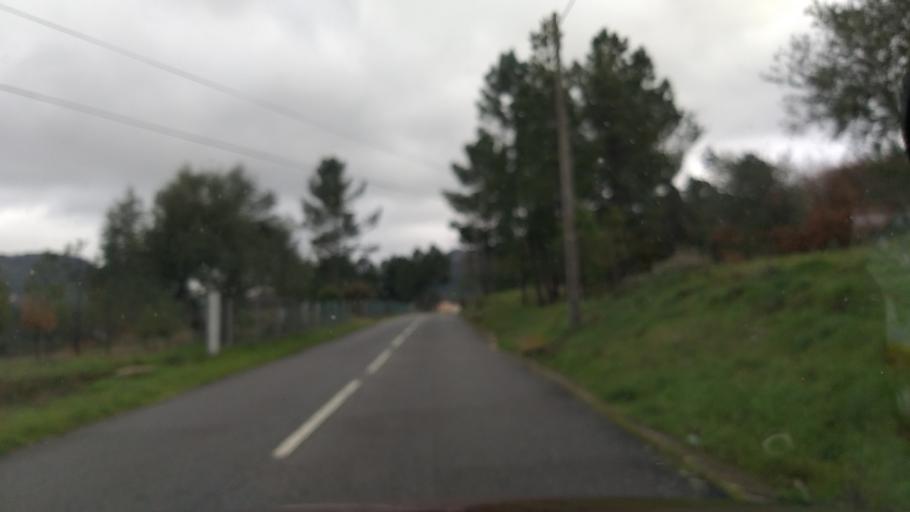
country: PT
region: Guarda
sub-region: Celorico da Beira
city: Celorico da Beira
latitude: 40.7061
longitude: -7.4401
